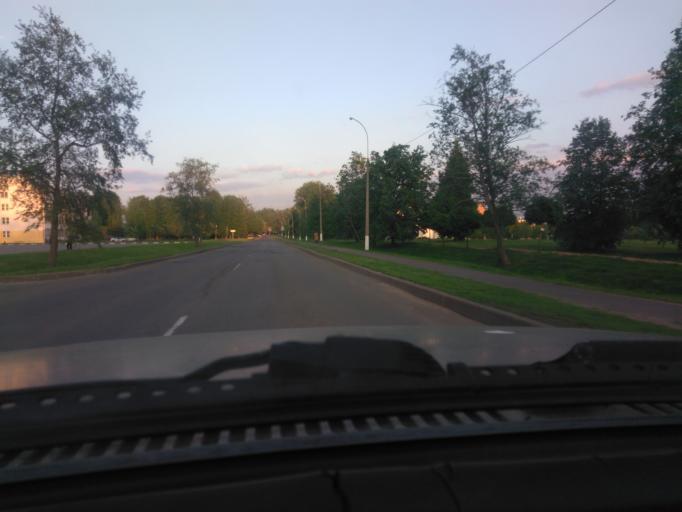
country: BY
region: Mogilev
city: Mahilyow
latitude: 53.9296
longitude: 30.3070
